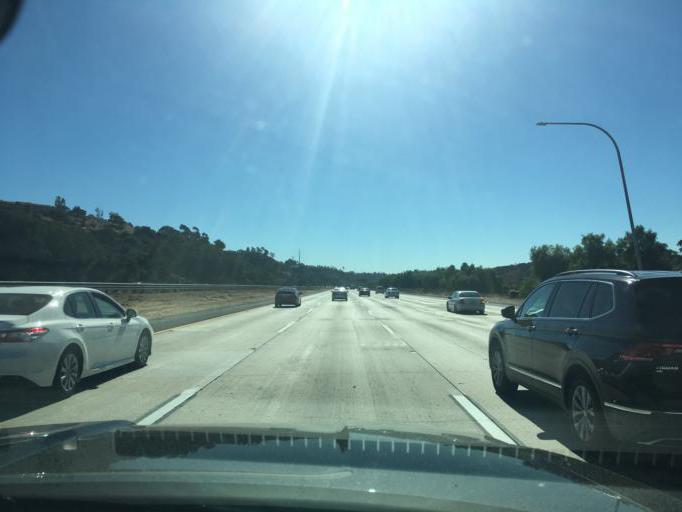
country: US
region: California
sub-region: San Diego County
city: La Mesa
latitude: 32.8068
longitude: -117.1137
